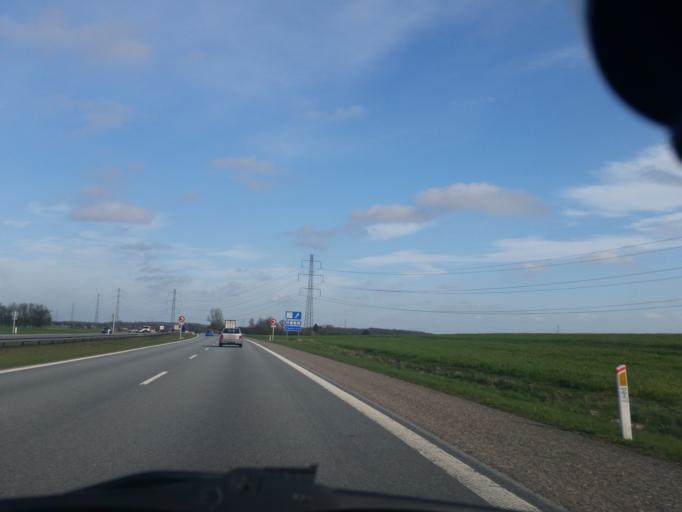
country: DK
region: Zealand
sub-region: Ringsted Kommune
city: Ringsted
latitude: 55.4542
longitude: 11.8486
